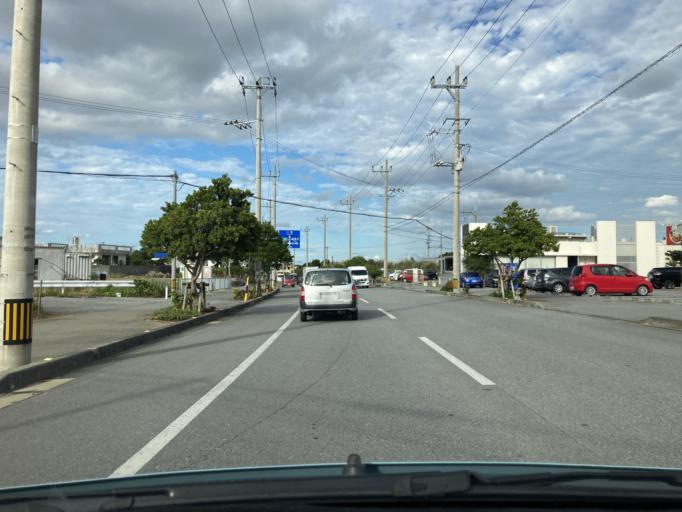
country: JP
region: Okinawa
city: Gushikawa
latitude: 26.3700
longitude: 127.8264
